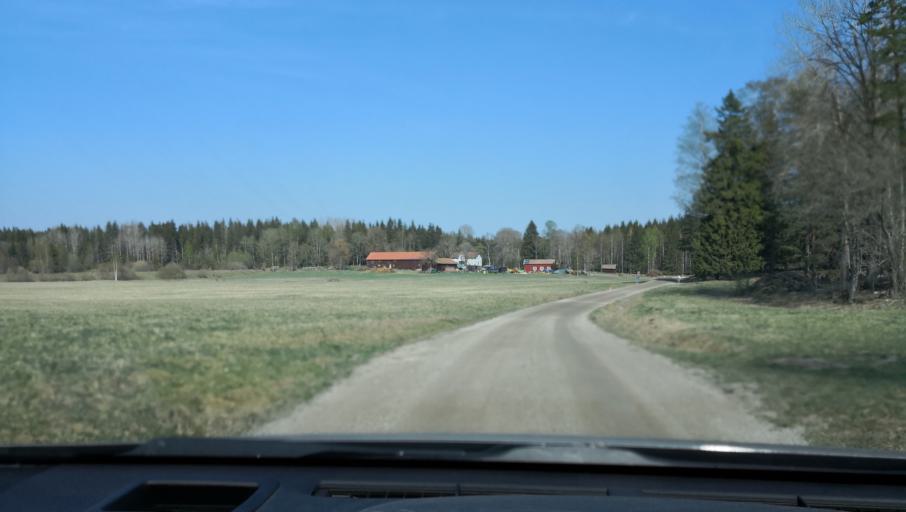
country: SE
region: Uppsala
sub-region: Heby Kommun
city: Heby
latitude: 60.0100
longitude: 16.7322
